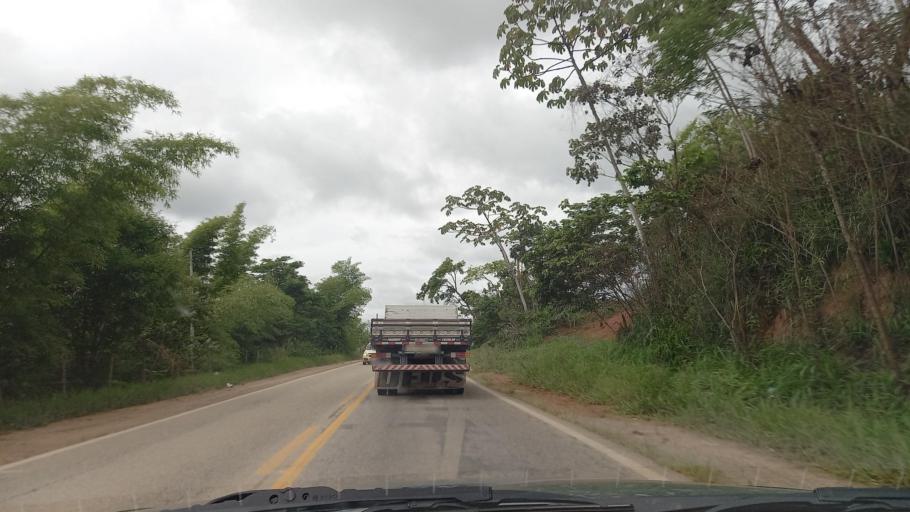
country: BR
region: Pernambuco
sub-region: Canhotinho
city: Canhotinho
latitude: -8.8555
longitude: -36.1730
